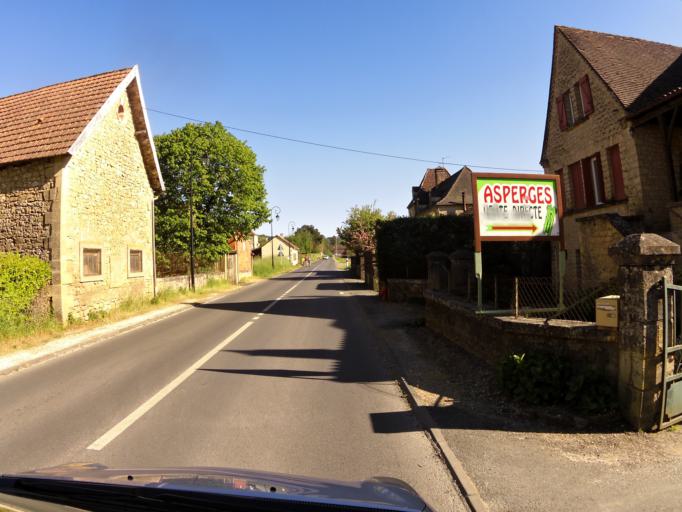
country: FR
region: Aquitaine
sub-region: Departement de la Dordogne
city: Cenac-et-Saint-Julien
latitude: 44.8217
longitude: 1.1884
